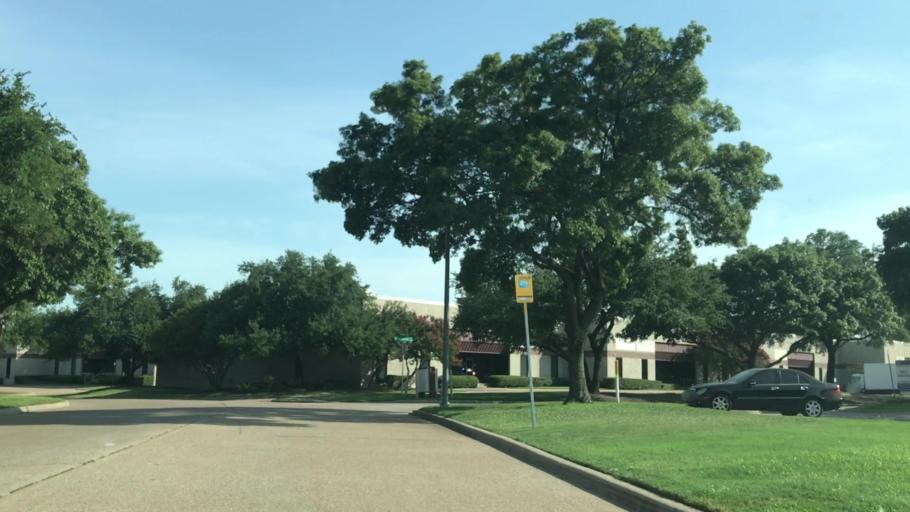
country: US
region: Texas
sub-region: Dallas County
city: Richardson
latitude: 32.8938
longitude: -96.7064
